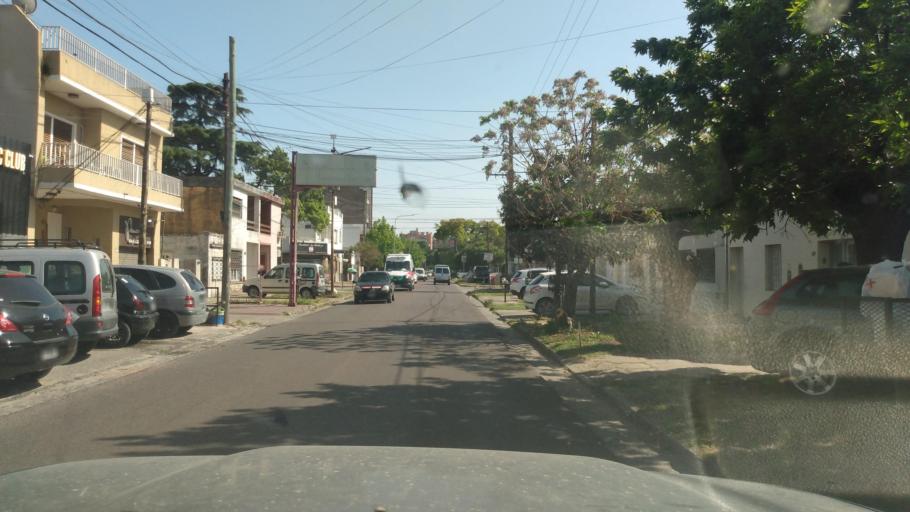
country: AR
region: Buenos Aires
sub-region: Partido de Moron
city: Moron
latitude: -34.6396
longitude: -58.5959
